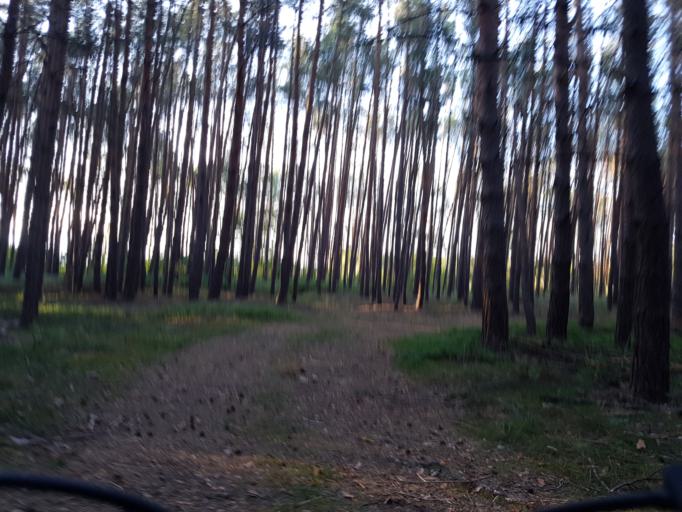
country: DE
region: Brandenburg
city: Schilda
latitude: 51.5883
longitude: 13.3509
